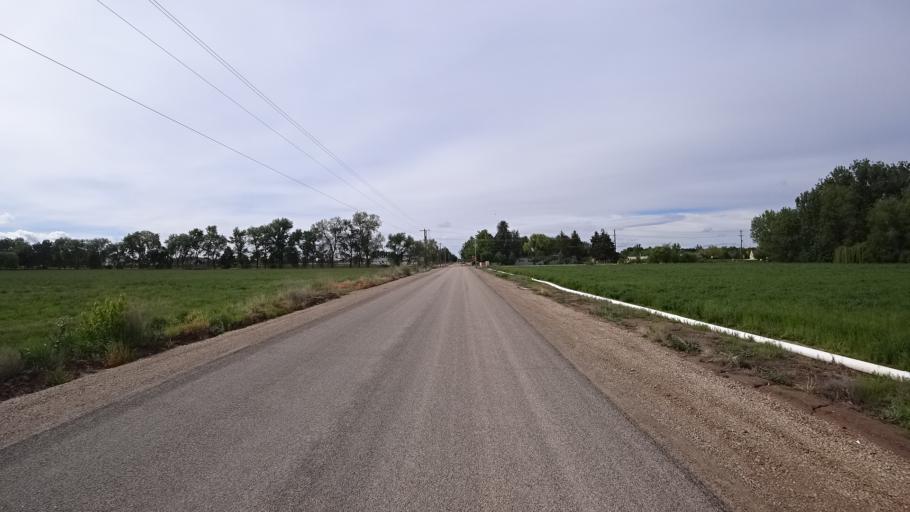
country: US
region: Idaho
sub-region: Ada County
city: Eagle
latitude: 43.7221
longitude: -116.4035
